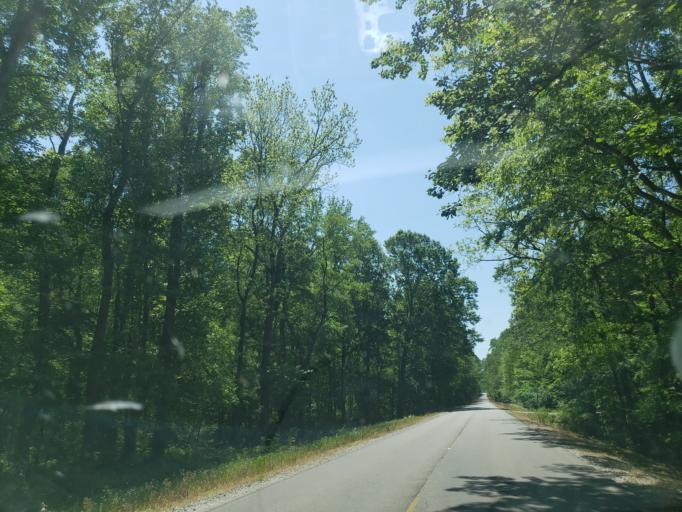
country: US
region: Alabama
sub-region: Madison County
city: Harvest
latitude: 34.9190
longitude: -86.7303
